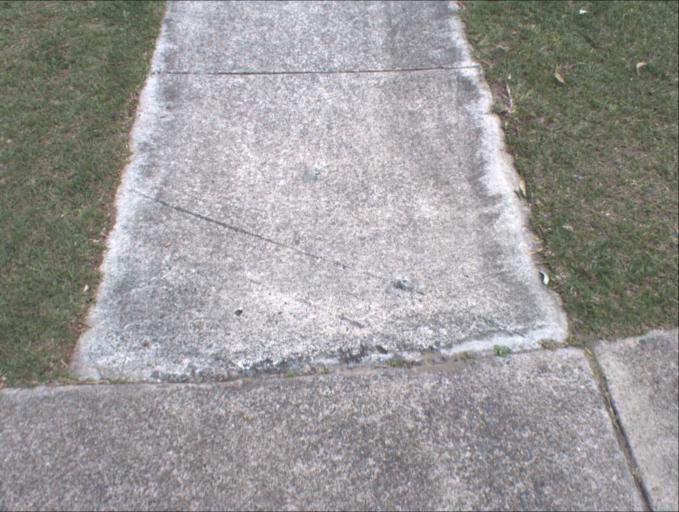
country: AU
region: Queensland
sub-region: Logan
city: Logan Reserve
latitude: -27.6878
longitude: 153.0796
